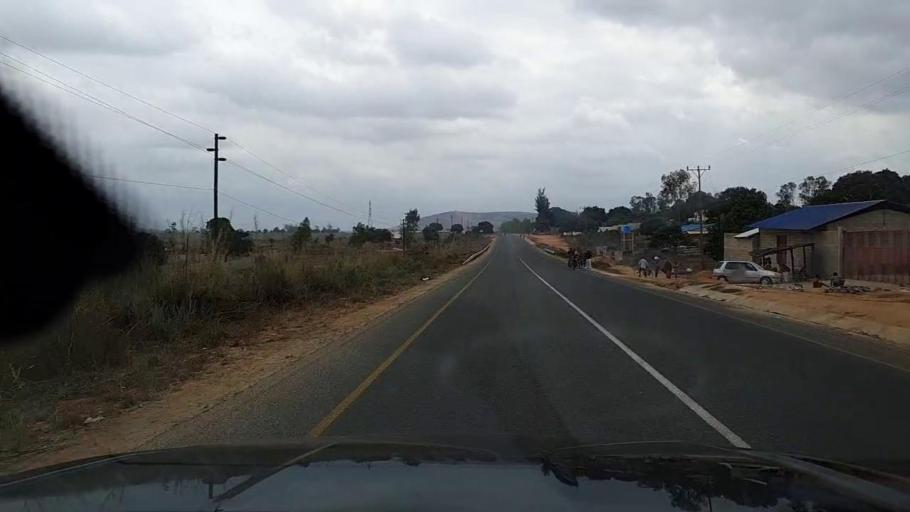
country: MZ
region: Nampula
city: Nampula
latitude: -15.1712
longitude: 39.3081
